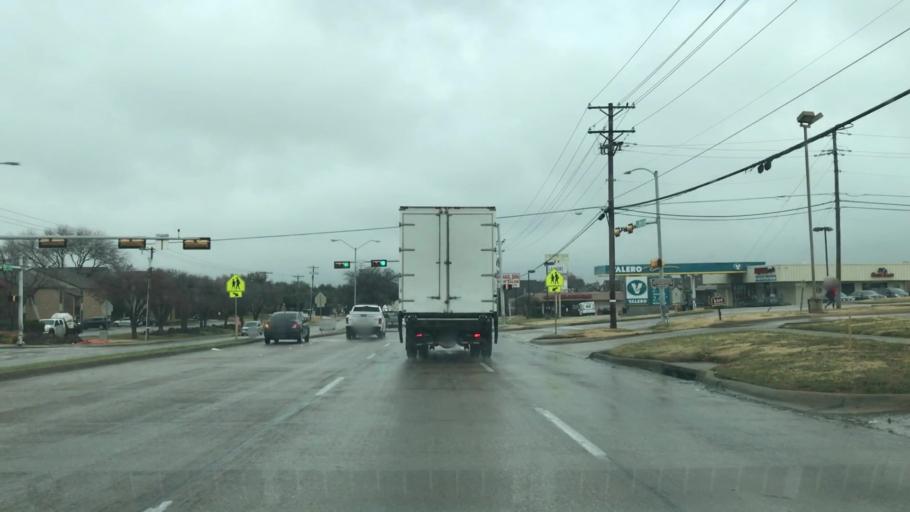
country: US
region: Texas
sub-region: Dallas County
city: Irving
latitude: 32.8603
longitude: -96.9918
